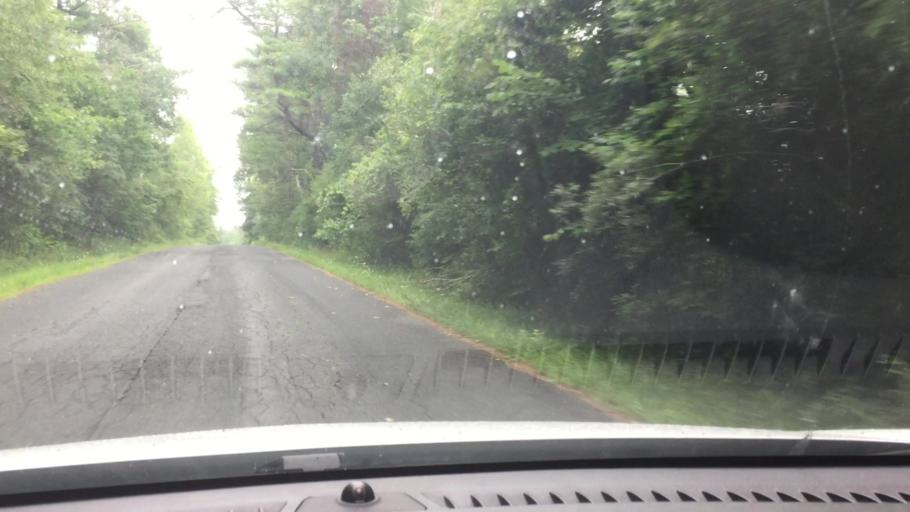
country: US
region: Massachusetts
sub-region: Berkshire County
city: Lee
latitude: 42.3113
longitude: -73.2849
